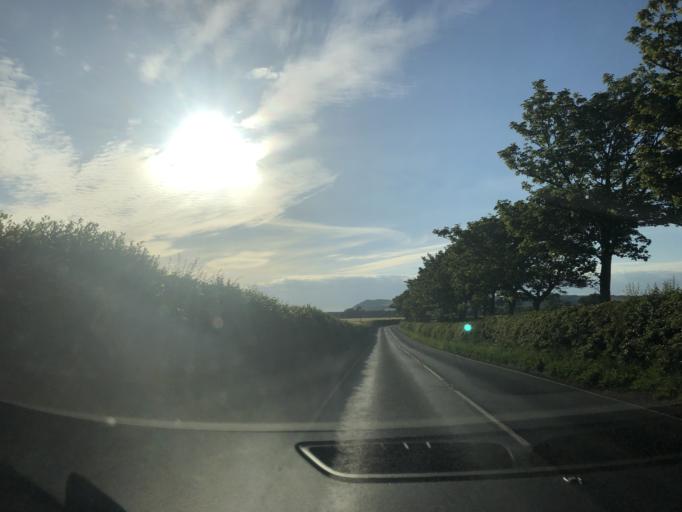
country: GB
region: Scotland
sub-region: Fife
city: Saint Monance
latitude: 56.1966
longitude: -2.8263
